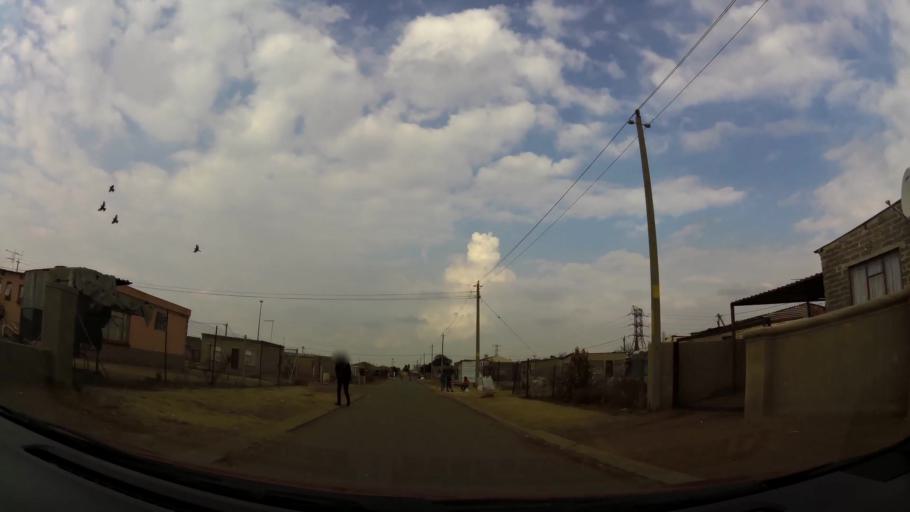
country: ZA
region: Gauteng
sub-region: Sedibeng District Municipality
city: Vanderbijlpark
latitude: -26.6764
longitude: 27.8558
